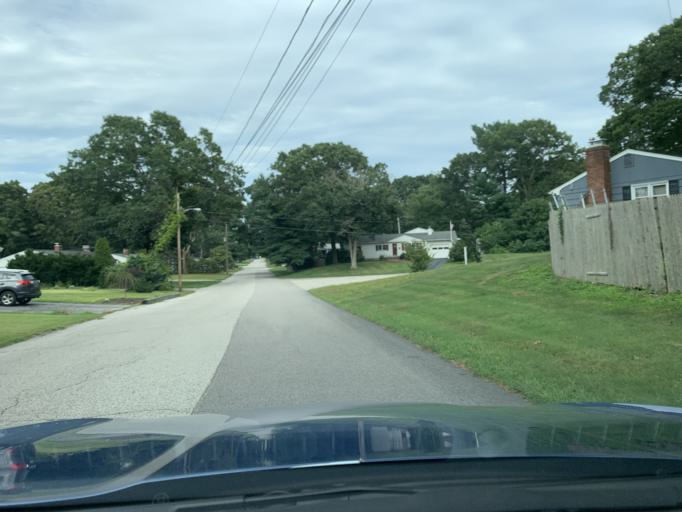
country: US
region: Rhode Island
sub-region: Kent County
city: East Greenwich
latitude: 41.6182
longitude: -71.4549
